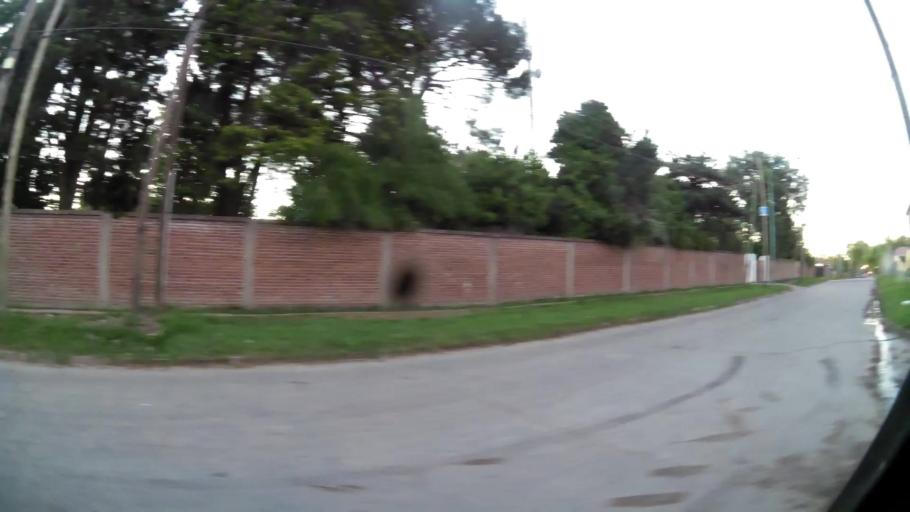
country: AR
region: Buenos Aires
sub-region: Partido de Almirante Brown
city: Adrogue
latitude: -34.7939
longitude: -58.3233
